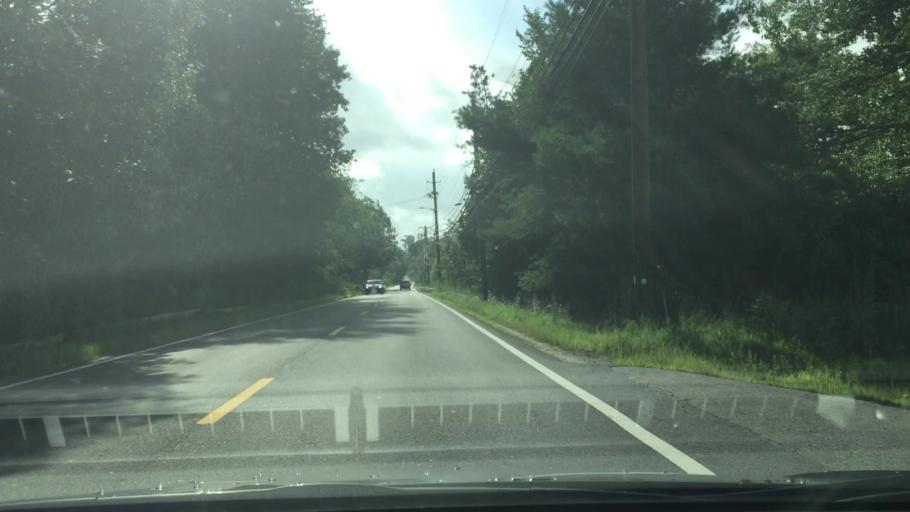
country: US
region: Massachusetts
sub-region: Middlesex County
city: Stow
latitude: 42.4789
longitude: -71.4920
